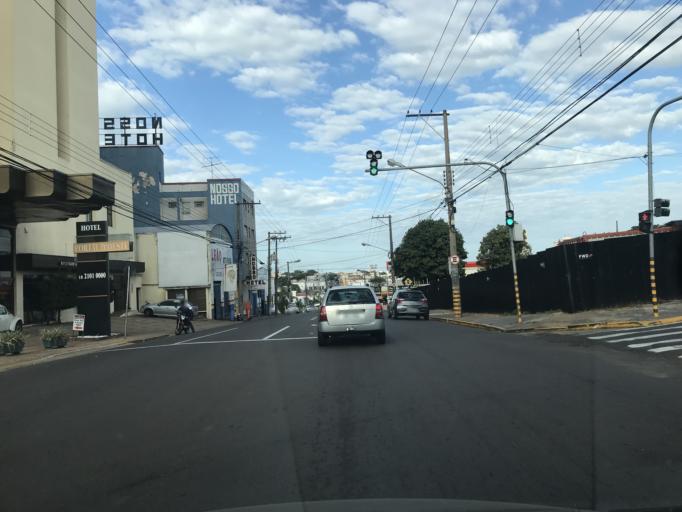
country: BR
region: Sao Paulo
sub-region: Presidente Prudente
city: Presidente Prudente
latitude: -22.1320
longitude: -51.3878
